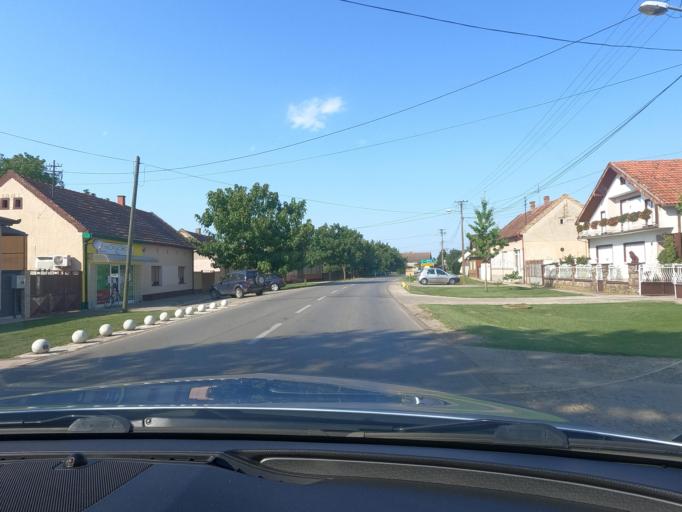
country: RS
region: Autonomna Pokrajina Vojvodina
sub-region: Juznobacki Okrug
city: Kovilj
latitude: 45.2358
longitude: 20.0281
